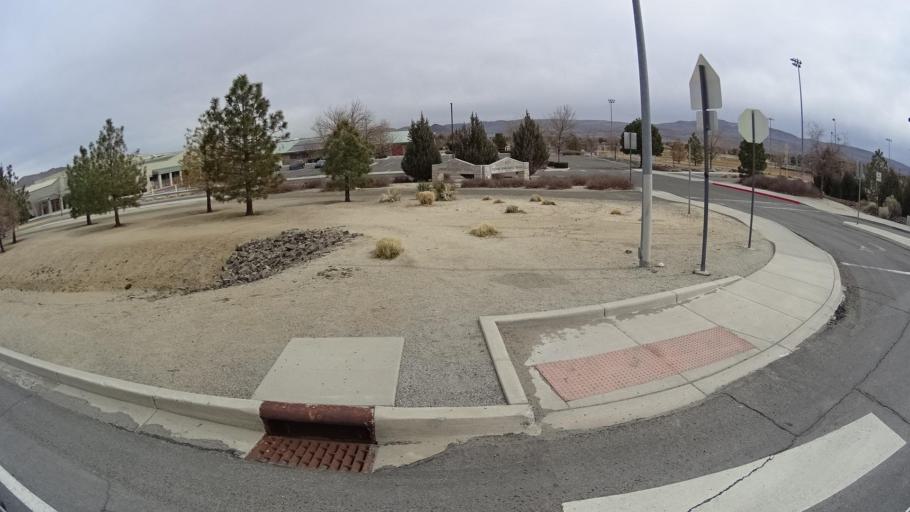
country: US
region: Nevada
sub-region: Washoe County
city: Spanish Springs
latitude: 39.6463
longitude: -119.7236
